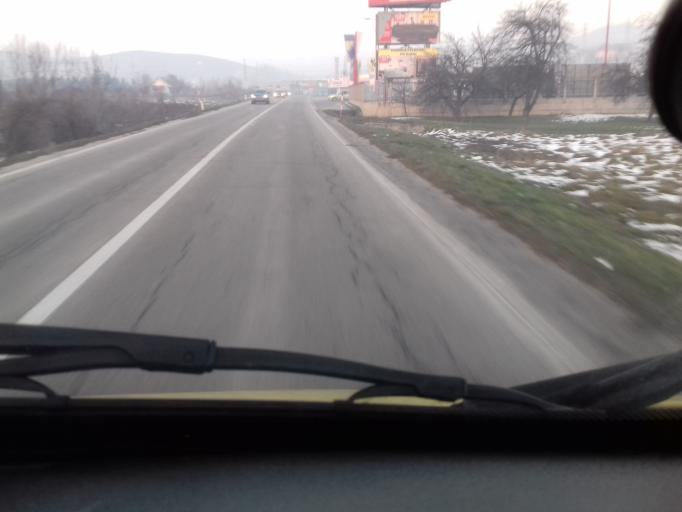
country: BA
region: Federation of Bosnia and Herzegovina
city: Vogosca
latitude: 43.8771
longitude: 18.3131
